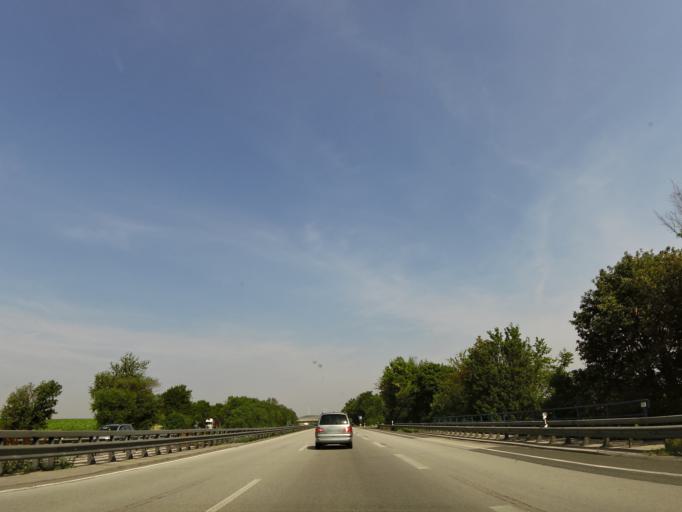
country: DE
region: Rheinland-Pfalz
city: Gundheim
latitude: 49.6885
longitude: 8.2404
